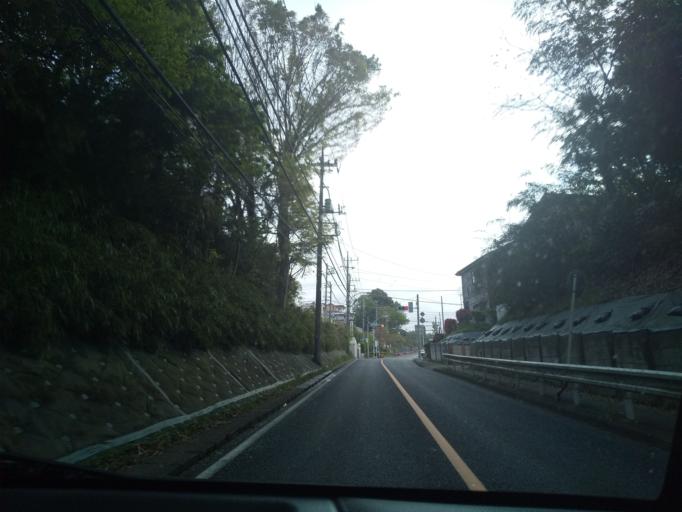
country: JP
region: Tokyo
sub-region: Machida-shi
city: Machida
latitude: 35.5944
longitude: 139.4576
